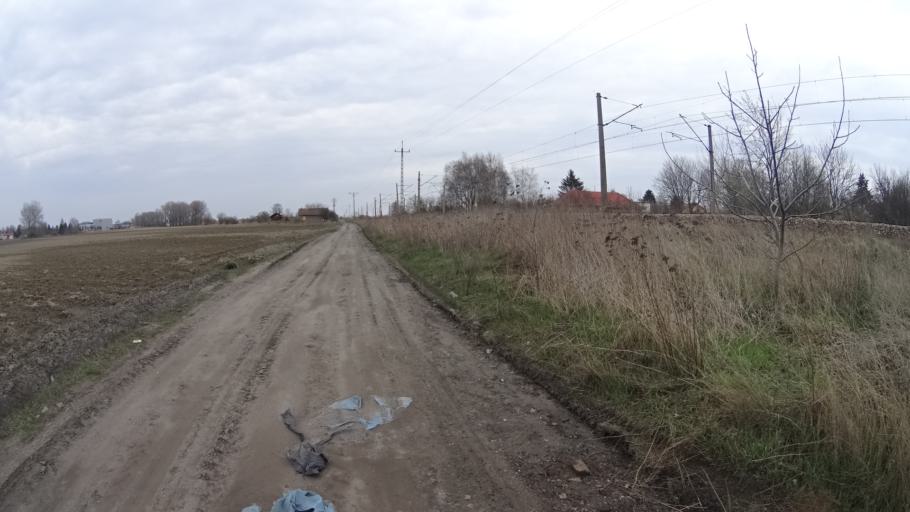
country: PL
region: Masovian Voivodeship
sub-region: Powiat warszawski zachodni
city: Jozefow
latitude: 52.2035
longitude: 20.7210
